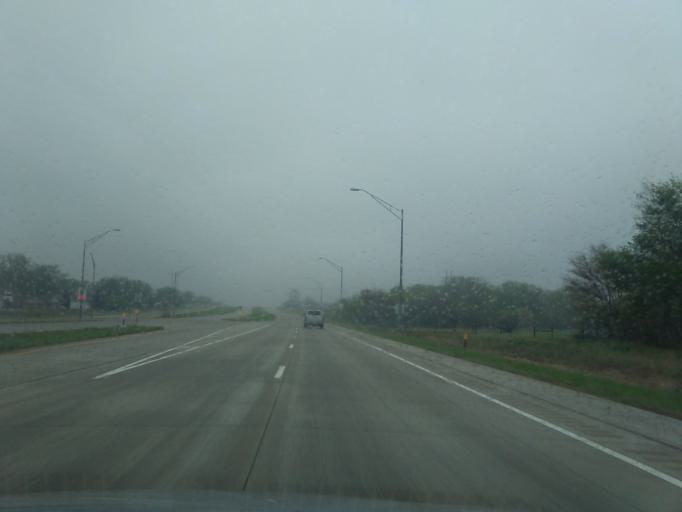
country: US
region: Nebraska
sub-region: Madison County
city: Norfolk
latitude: 42.0598
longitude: -97.3535
